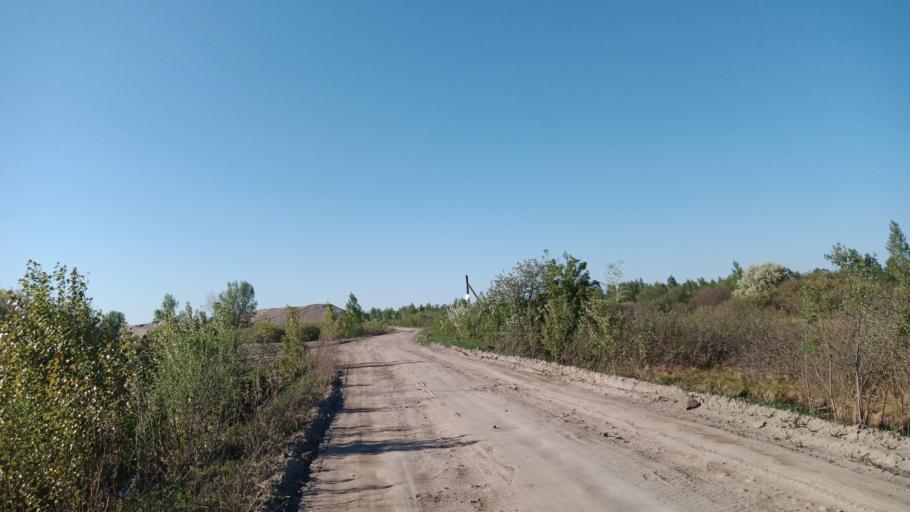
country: RU
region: Altai Krai
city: Zaton
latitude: 53.3076
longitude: 83.8241
